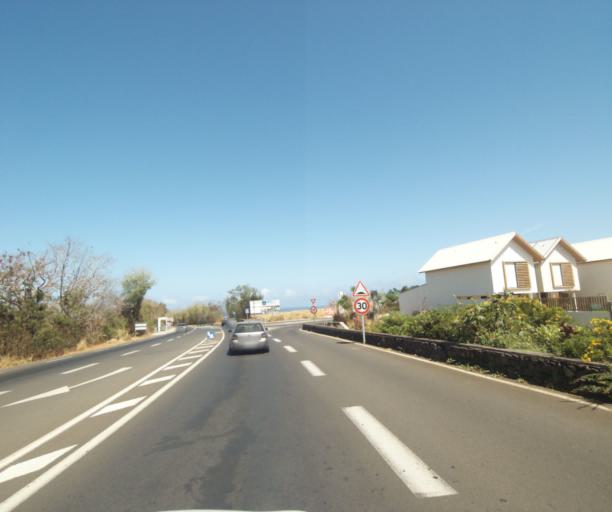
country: RE
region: Reunion
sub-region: Reunion
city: Le Port
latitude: -20.9810
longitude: 55.3160
